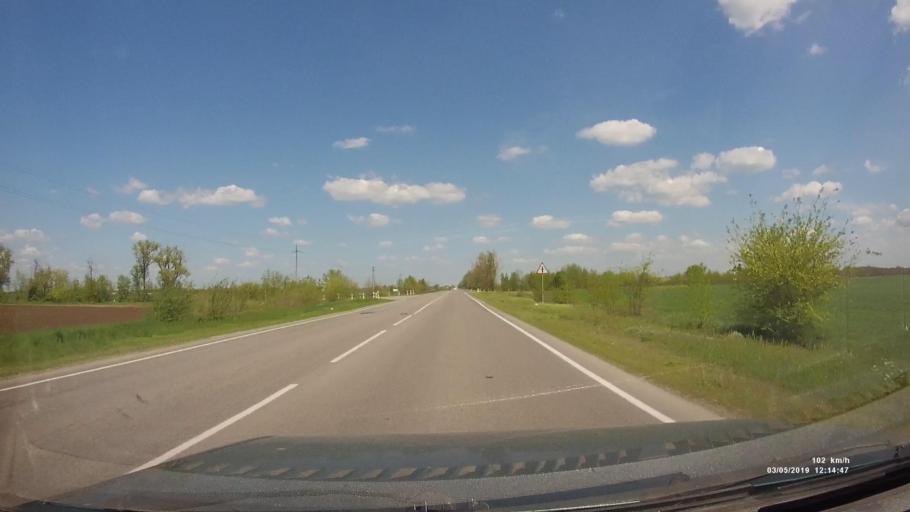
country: RU
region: Rostov
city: Melikhovskaya
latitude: 47.3489
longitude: 40.5671
